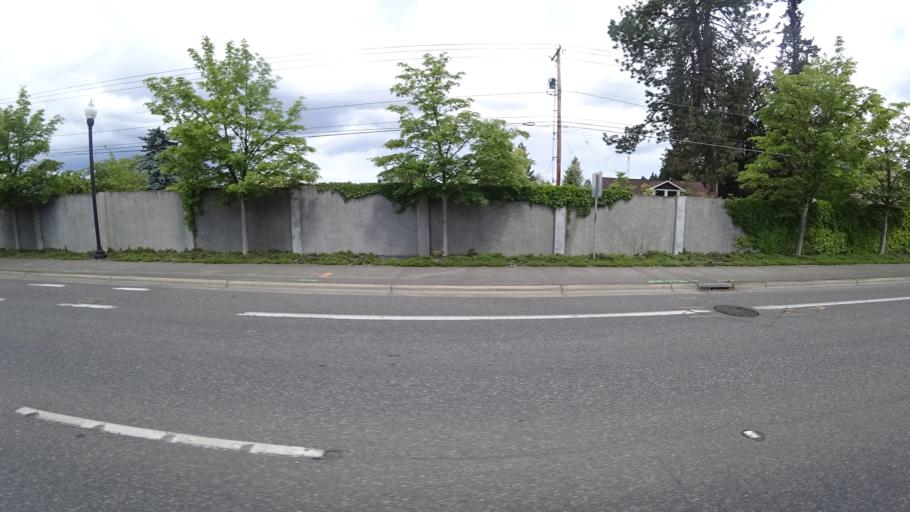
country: US
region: Oregon
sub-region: Washington County
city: Aloha
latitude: 45.4825
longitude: -122.8497
